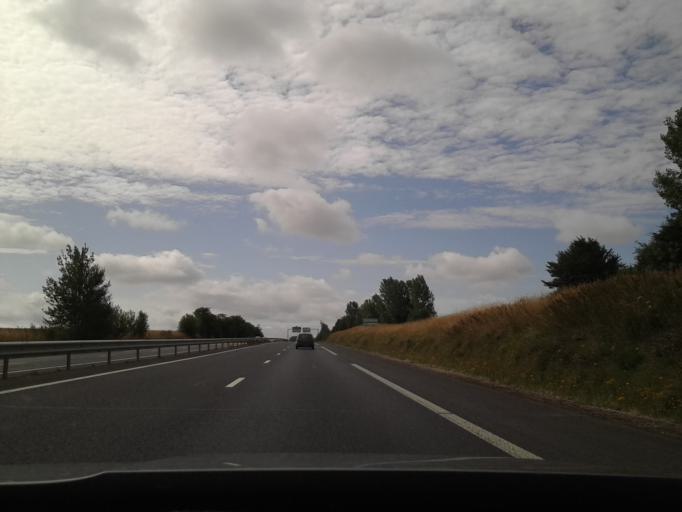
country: FR
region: Lower Normandy
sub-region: Departement du Calvados
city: Potigny
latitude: 48.9883
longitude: -0.2513
